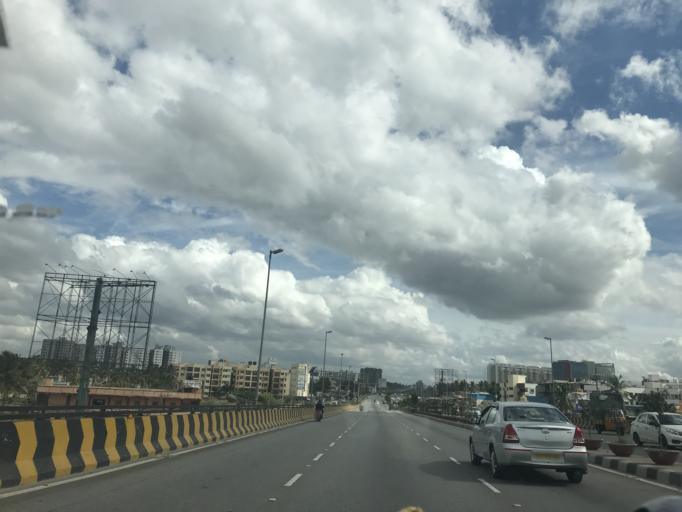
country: IN
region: Karnataka
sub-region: Bangalore Urban
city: Yelahanka
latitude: 13.1023
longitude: 77.6001
